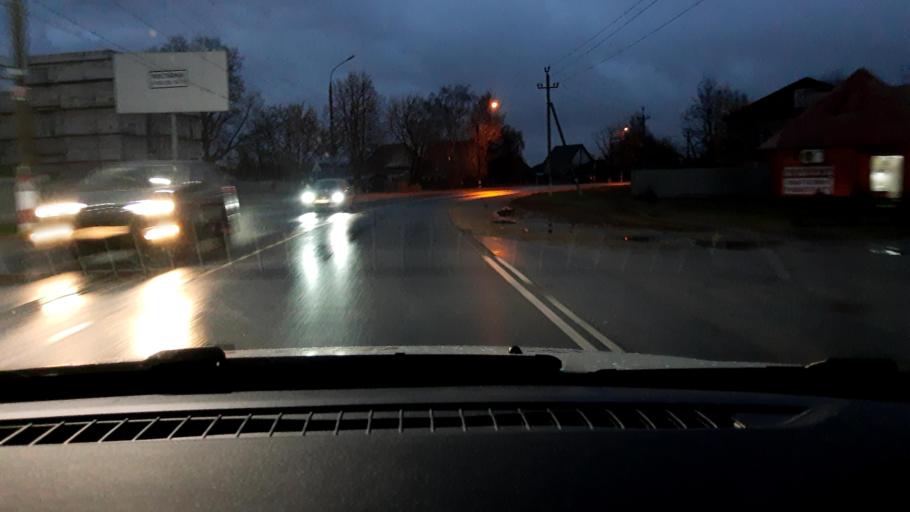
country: RU
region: Nizjnij Novgorod
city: Bor
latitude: 56.3760
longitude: 44.0309
